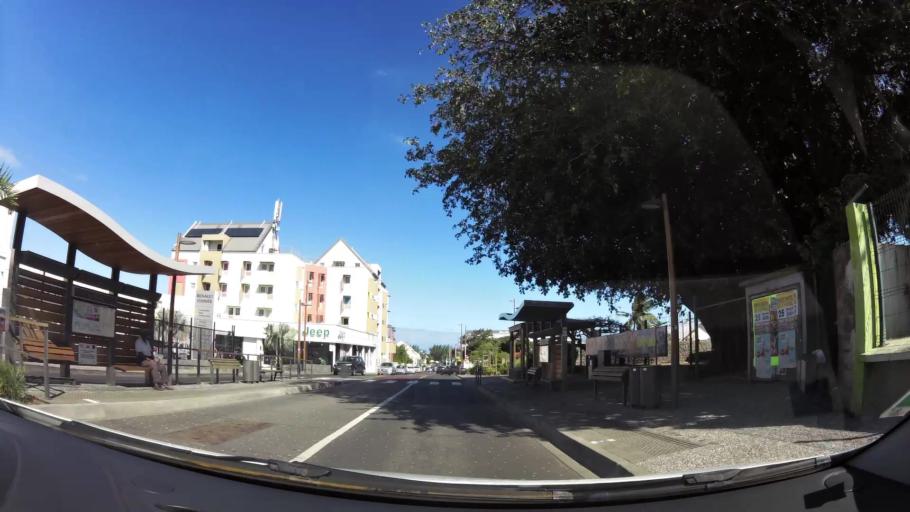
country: RE
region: Reunion
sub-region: Reunion
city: Saint-Pierre
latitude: -21.3344
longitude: 55.4600
